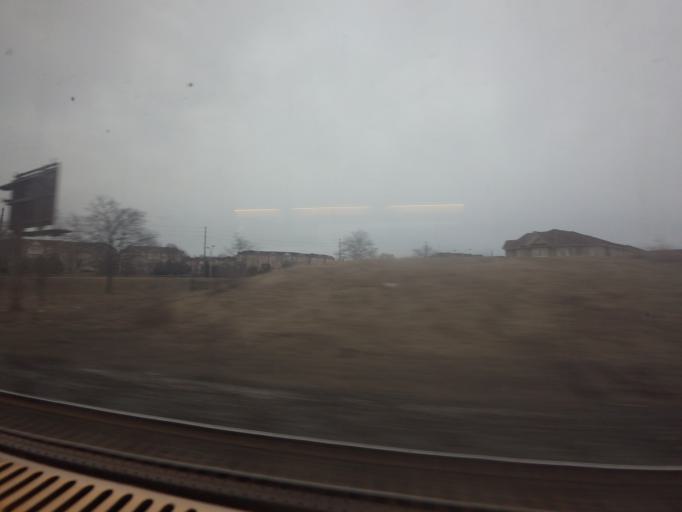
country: CA
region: Ontario
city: Scarborough
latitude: 43.7206
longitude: -79.2529
